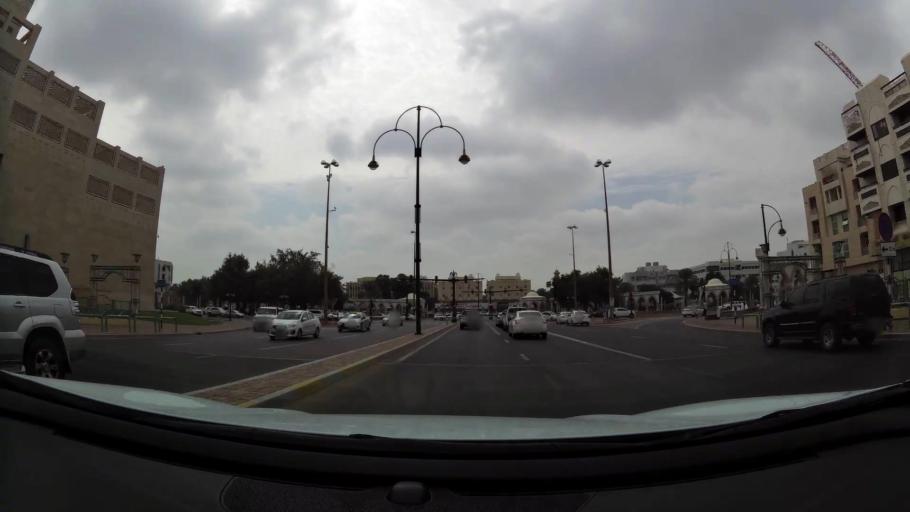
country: AE
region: Abu Dhabi
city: Al Ain
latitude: 24.2228
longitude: 55.7659
